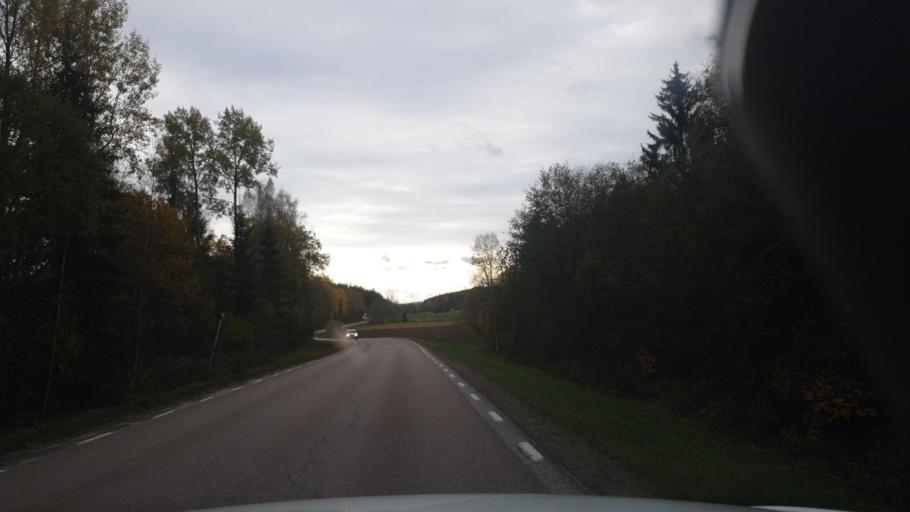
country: SE
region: Vaermland
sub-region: Arvika Kommun
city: Arvika
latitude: 59.6764
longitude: 12.7959
